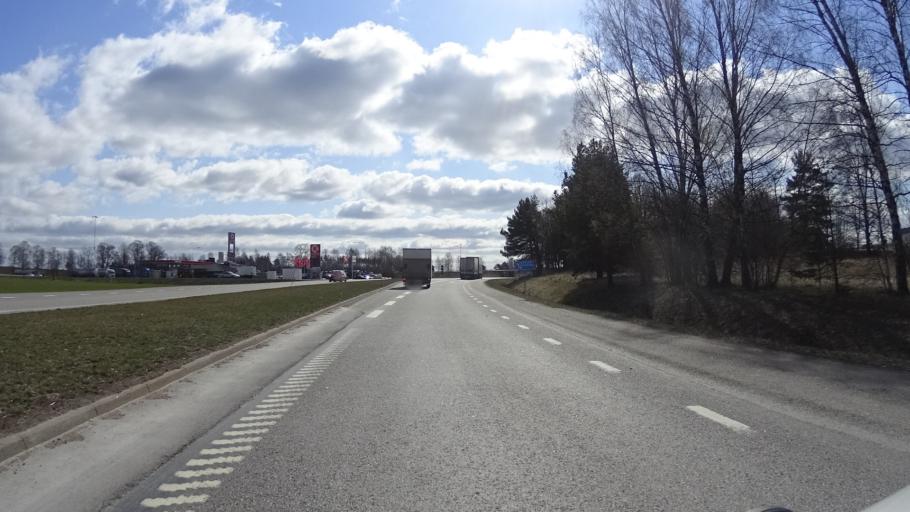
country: SE
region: OEstergoetland
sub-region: Mjolby Kommun
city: Mantorp
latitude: 58.3731
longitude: 15.2920
